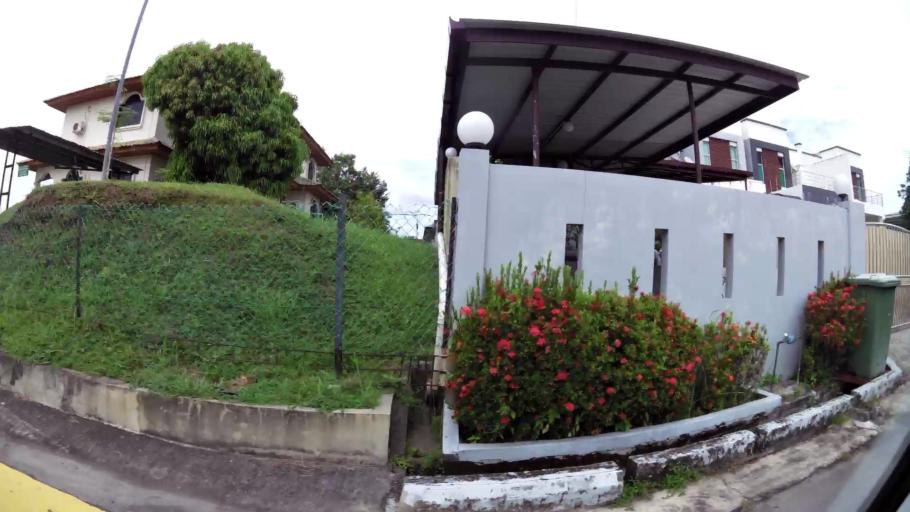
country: BN
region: Brunei and Muara
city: Bandar Seri Begawan
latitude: 4.8813
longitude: 114.8963
